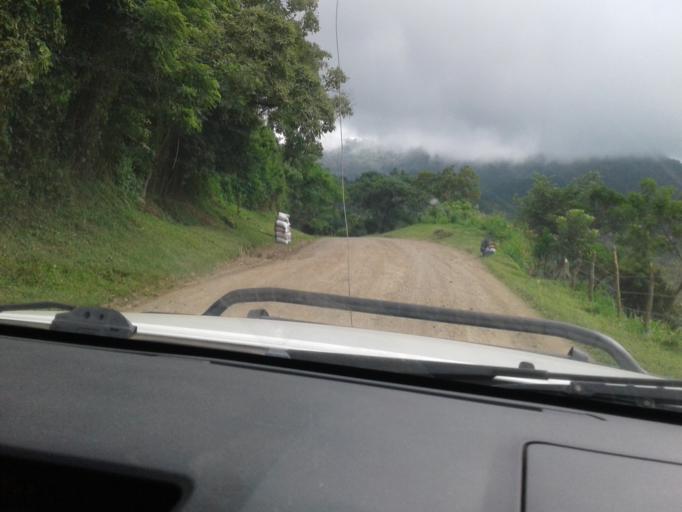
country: NI
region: Matagalpa
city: San Ramon
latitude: 12.9096
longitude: -85.7958
